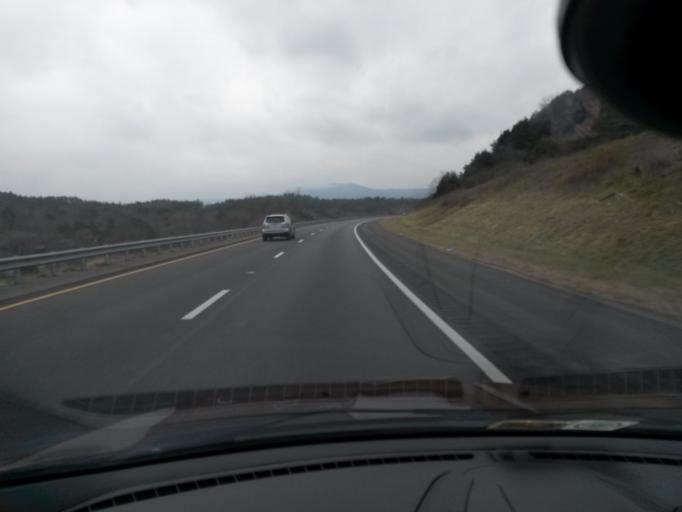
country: US
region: Virginia
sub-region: Alleghany County
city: Clifton Forge
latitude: 37.7957
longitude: -79.7187
